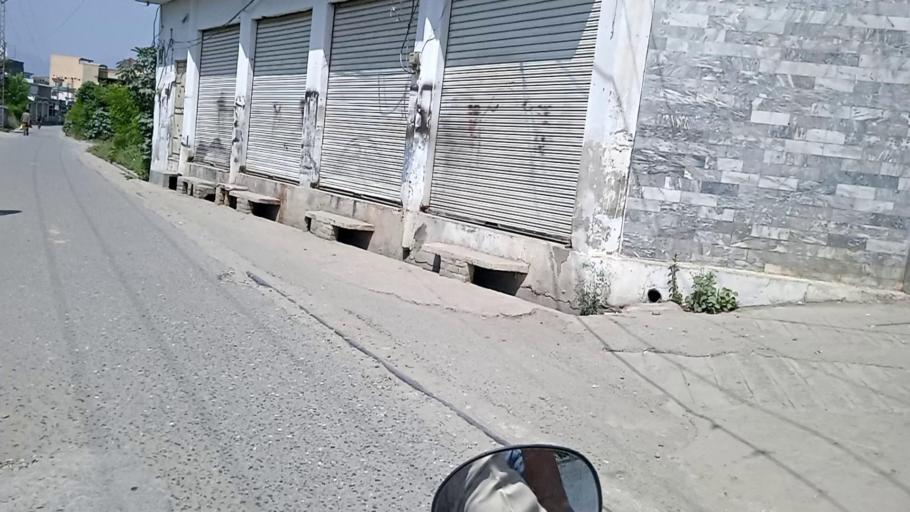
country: PK
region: Khyber Pakhtunkhwa
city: Mingora
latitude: 34.7784
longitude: 72.3555
